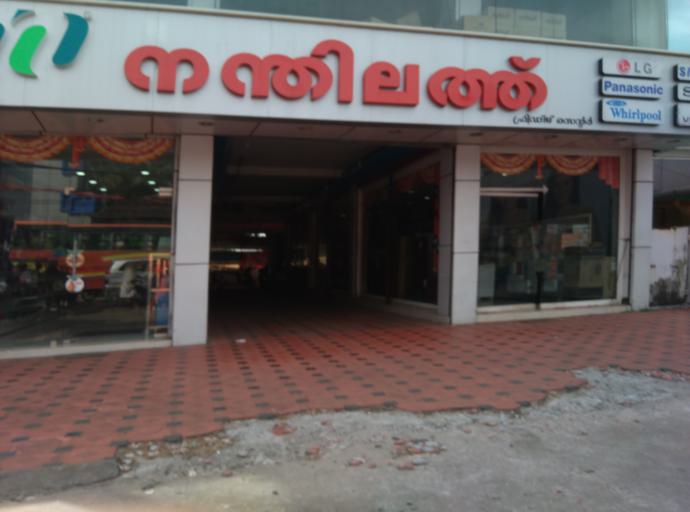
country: IN
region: Kerala
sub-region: Thrissur District
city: Trichur
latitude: 10.5232
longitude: 76.2076
